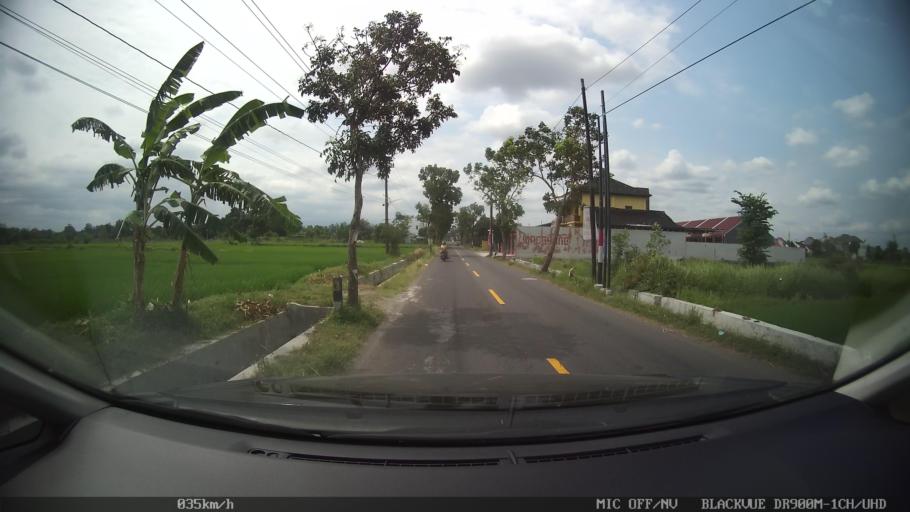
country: ID
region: Central Java
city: Candi Prambanan
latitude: -7.7519
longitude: 110.4809
